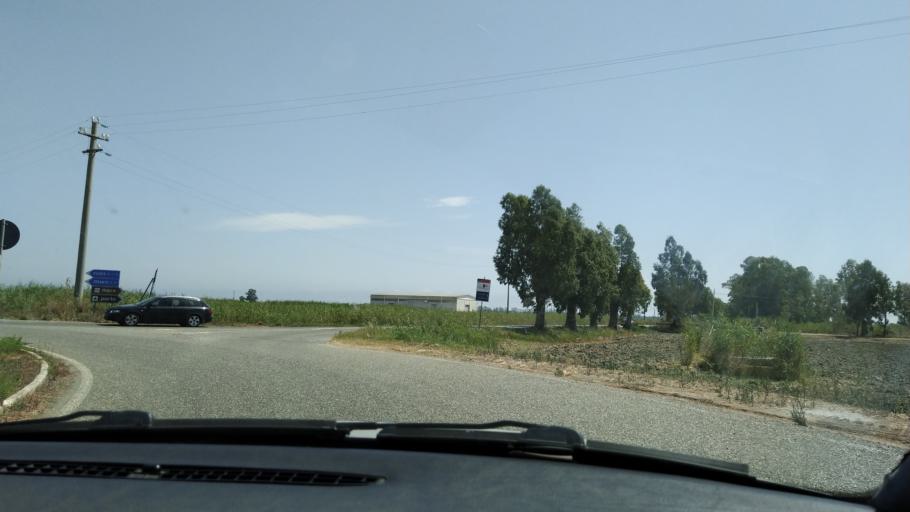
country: IT
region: Basilicate
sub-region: Provincia di Matera
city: Marconia
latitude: 40.3398
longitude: 16.7635
